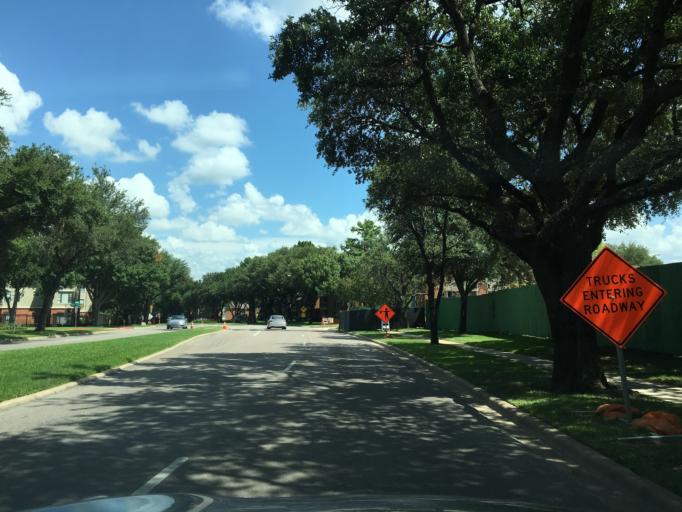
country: US
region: Texas
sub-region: Dallas County
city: University Park
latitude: 32.8599
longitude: -96.7611
